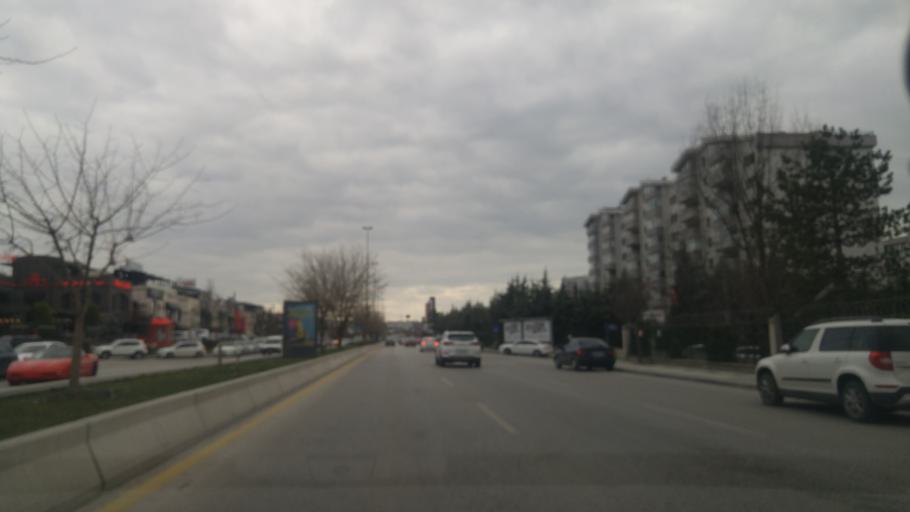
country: TR
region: Ankara
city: Etimesgut
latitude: 39.8718
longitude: 32.6875
